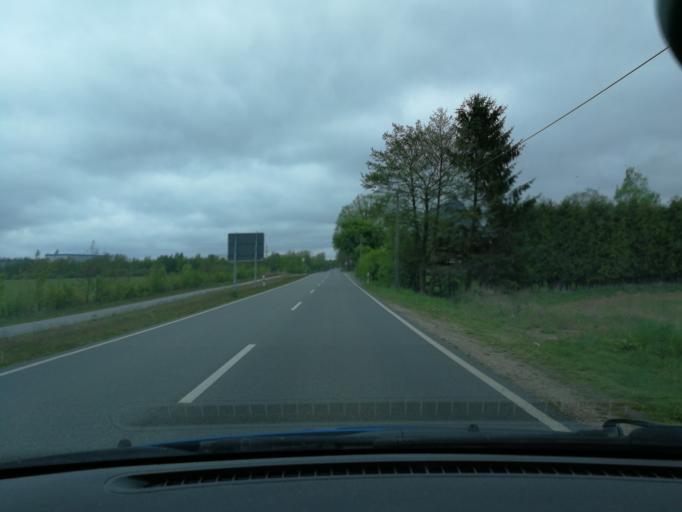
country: DE
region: Schleswig-Holstein
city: Hollenbek
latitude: 53.5017
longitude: 10.8366
